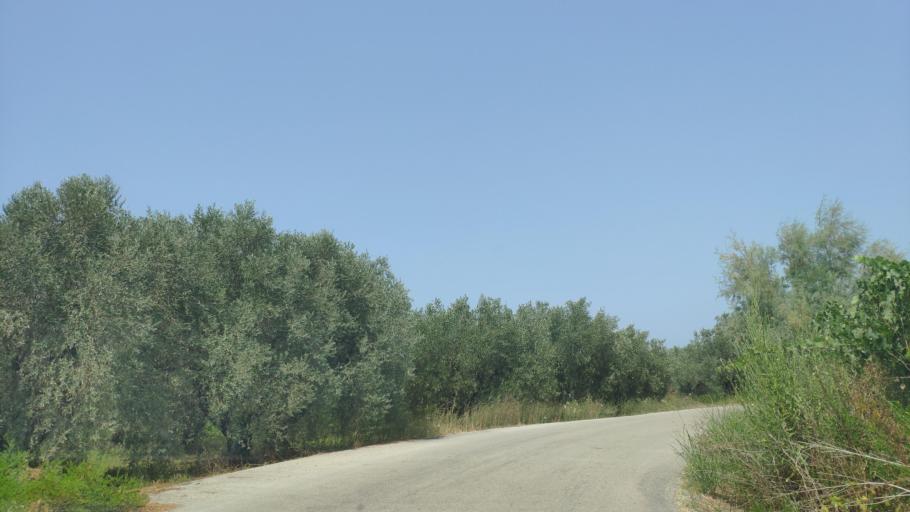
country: GR
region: Epirus
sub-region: Nomos Artas
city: Neochori
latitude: 39.0599
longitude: 21.0459
